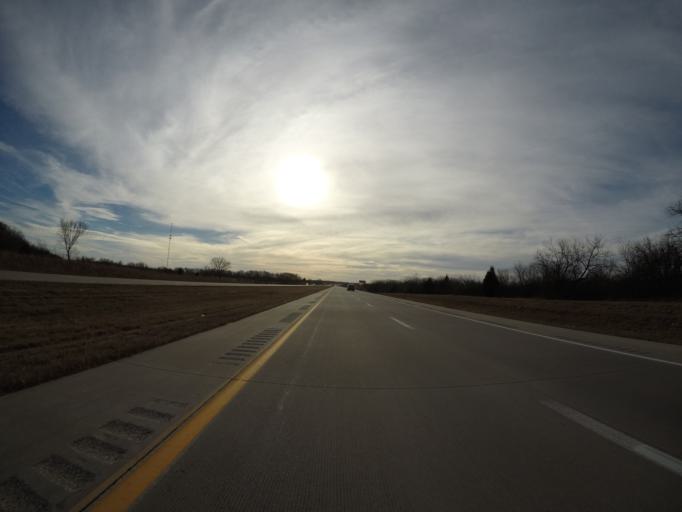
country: US
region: Kansas
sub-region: Franklin County
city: Wellsville
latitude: 38.7202
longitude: -95.0438
